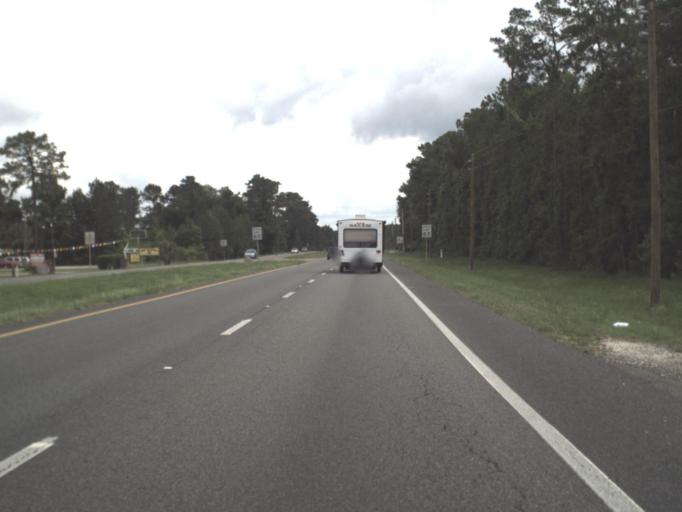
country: US
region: Florida
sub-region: Nassau County
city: Callahan
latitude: 30.5784
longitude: -81.8332
